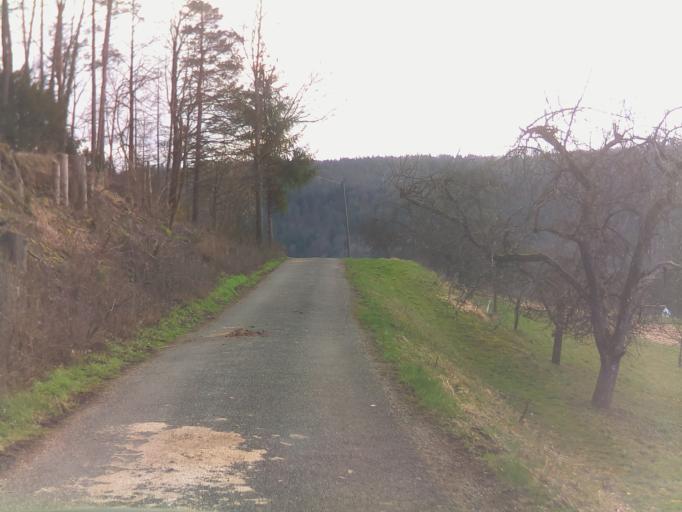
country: DE
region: Baden-Wuerttemberg
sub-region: Regierungsbezirk Stuttgart
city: Pluderhausen
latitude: 48.7903
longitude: 9.6158
